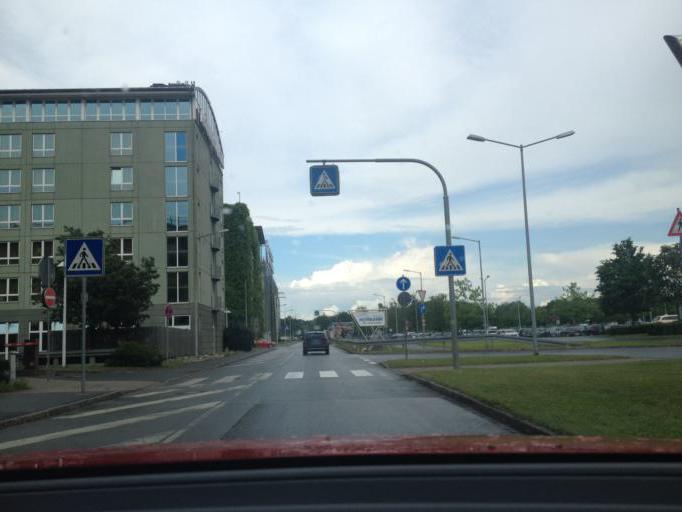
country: DE
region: Bavaria
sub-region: Regierungsbezirk Mittelfranken
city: Nuernberg
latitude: 49.4930
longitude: 11.0791
